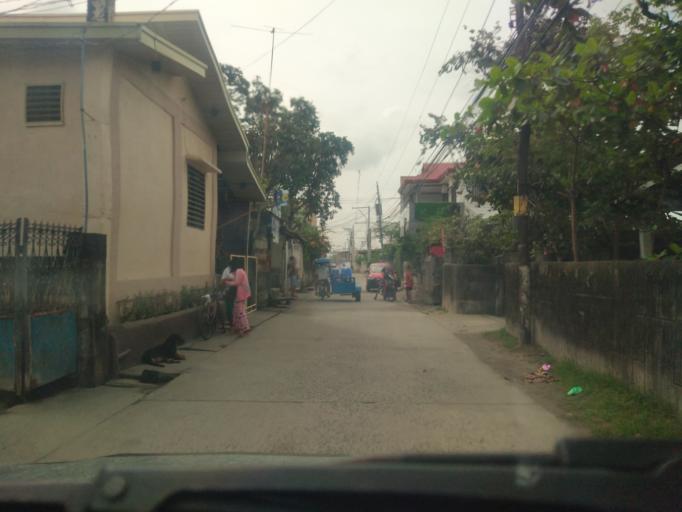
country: PH
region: Central Luzon
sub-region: Province of Pampanga
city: Pau
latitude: 15.0097
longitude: 120.7113
